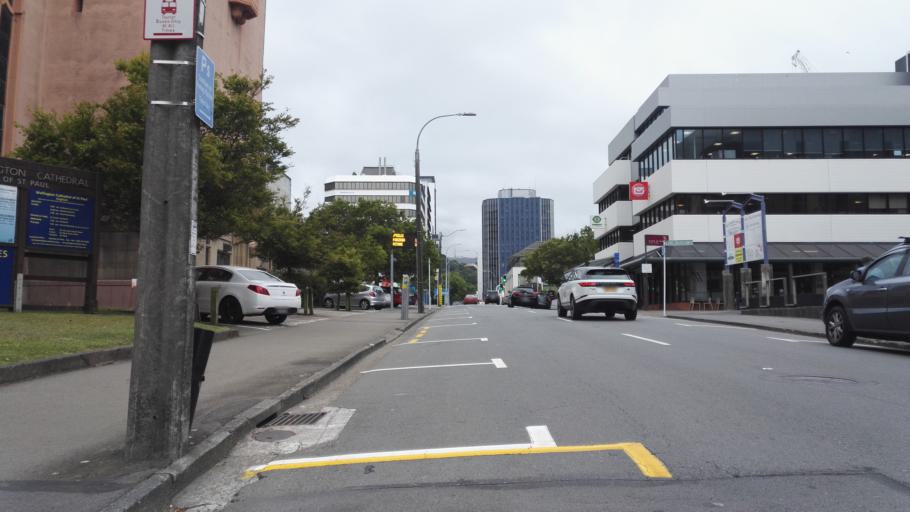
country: NZ
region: Wellington
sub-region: Wellington City
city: Wellington
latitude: -41.2765
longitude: 174.7778
